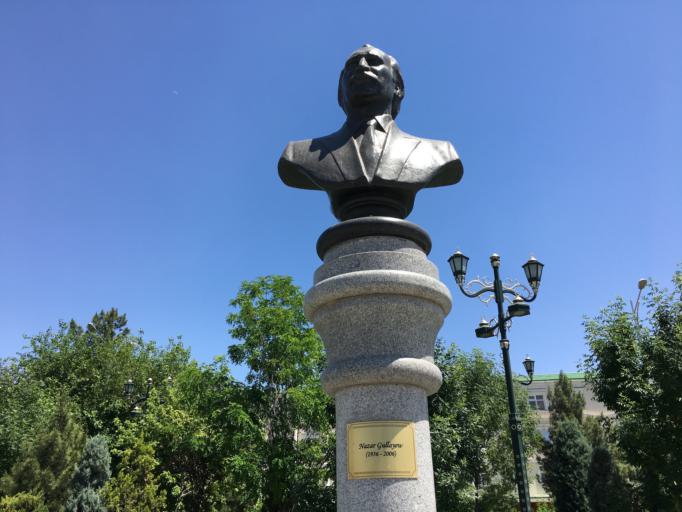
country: TM
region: Ahal
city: Ashgabat
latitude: 37.9463
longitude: 58.3783
